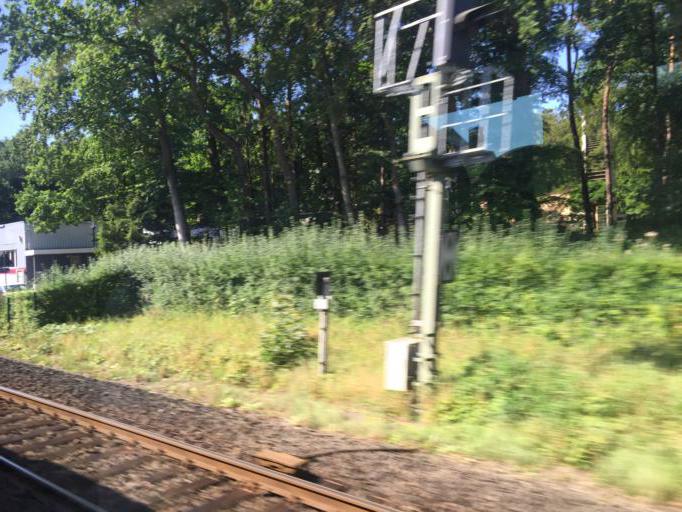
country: DE
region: Schleswig-Holstein
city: Bad Schwartau
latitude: 53.9193
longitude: 10.7062
